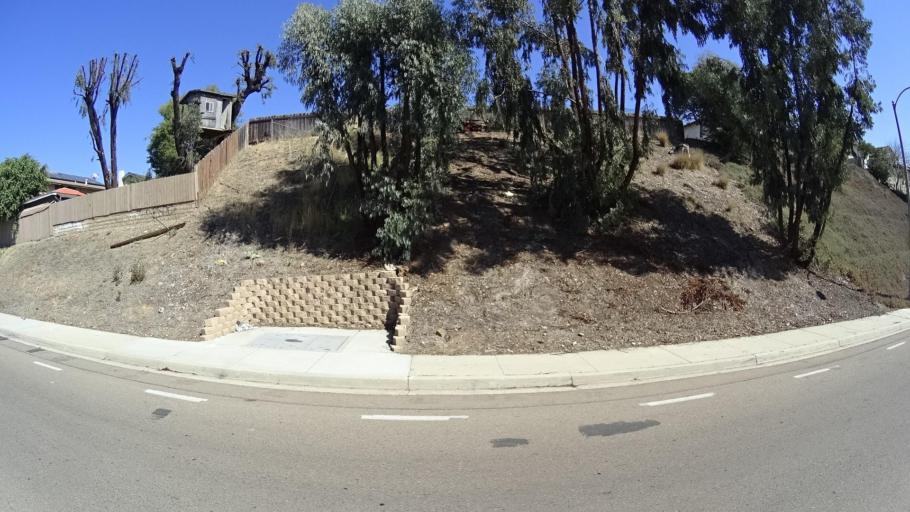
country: US
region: California
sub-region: San Diego County
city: La Presa
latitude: 32.6962
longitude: -117.0178
